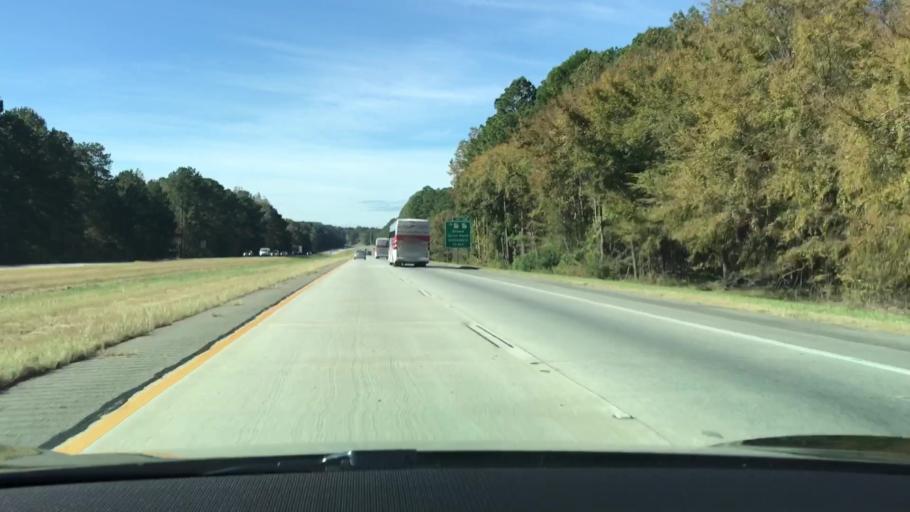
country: US
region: Georgia
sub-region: Greene County
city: Union Point
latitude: 33.5476
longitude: -83.0654
